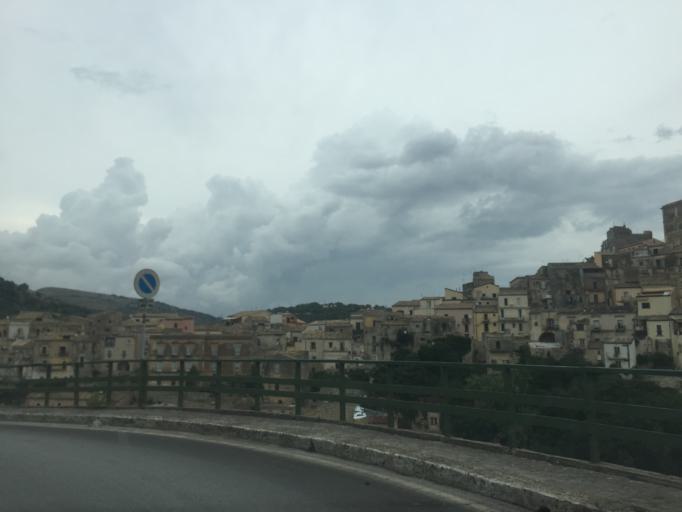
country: IT
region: Sicily
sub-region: Ragusa
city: Ragusa
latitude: 36.9247
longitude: 14.7382
